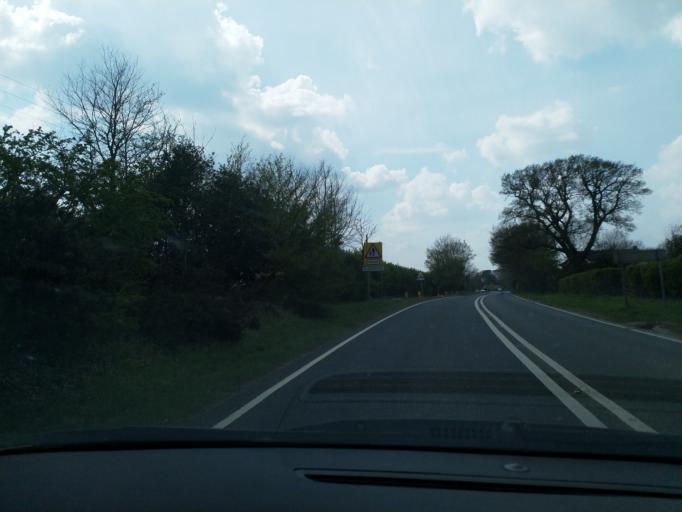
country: GB
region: England
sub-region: Warwickshire
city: Ryton on Dunsmore
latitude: 52.3488
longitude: -1.4620
